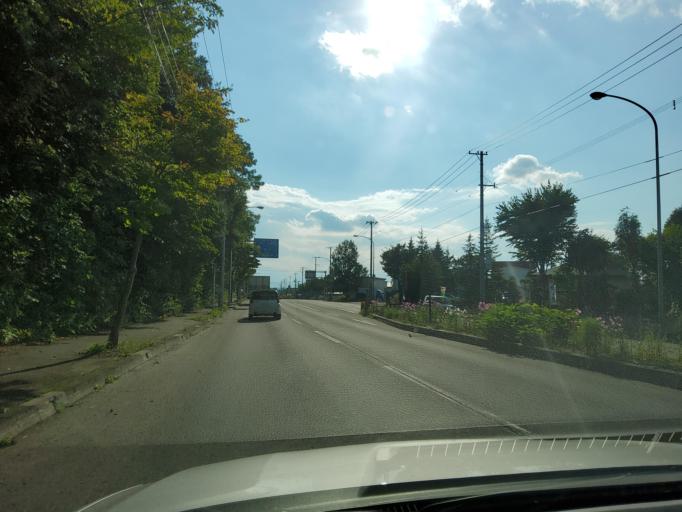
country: JP
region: Hokkaido
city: Obihiro
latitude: 42.9017
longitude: 143.2124
